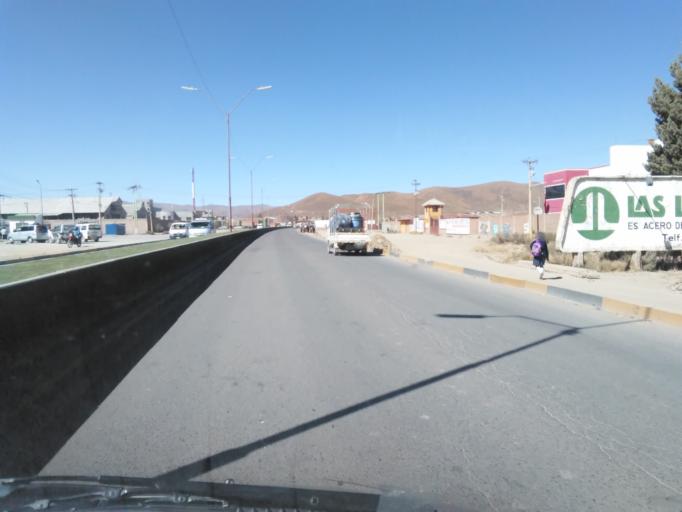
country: BO
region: Oruro
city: Oruro
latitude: -17.9775
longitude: -67.0602
